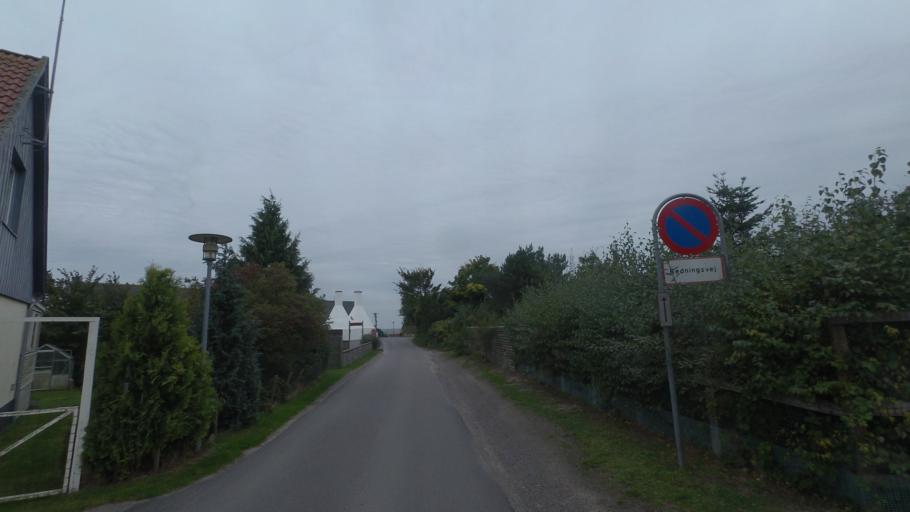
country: DK
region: Capital Region
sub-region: Bornholm Kommune
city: Akirkeby
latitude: 55.0014
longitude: 14.9910
